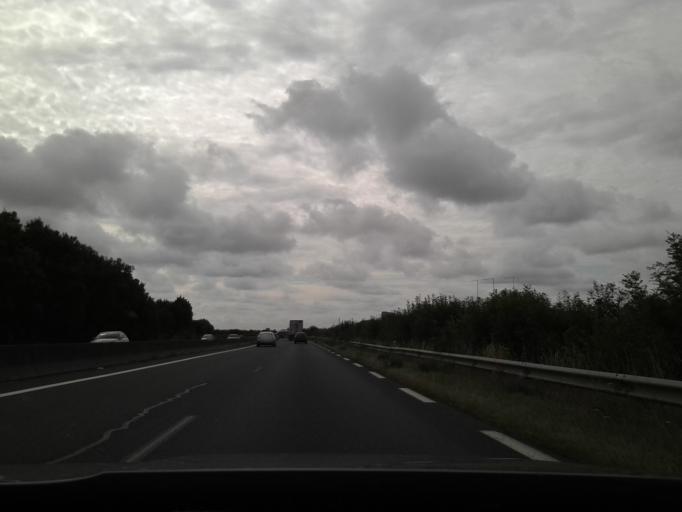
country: FR
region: Lower Normandy
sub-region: Departement du Calvados
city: Saint-Manvieu
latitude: 49.2112
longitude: -0.5205
